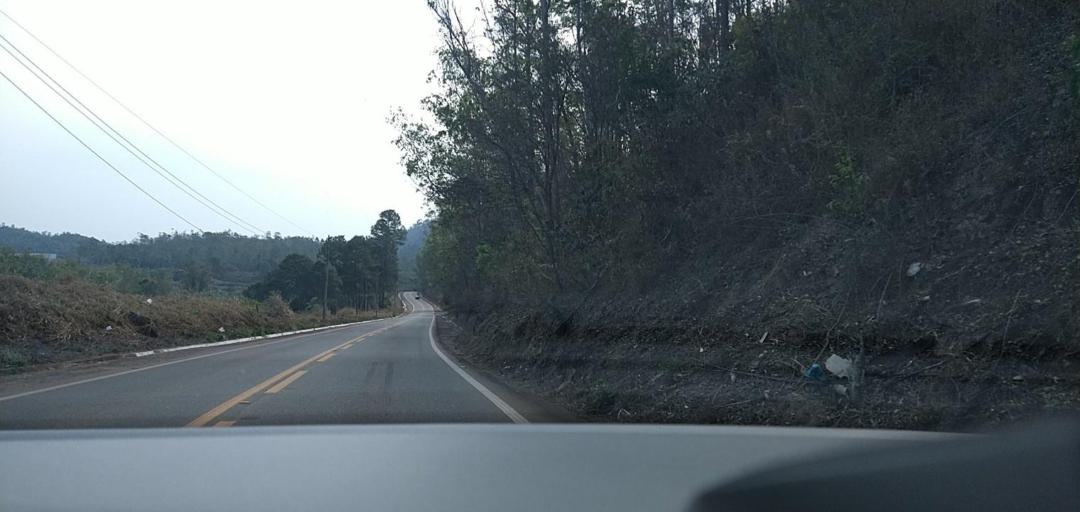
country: BR
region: Minas Gerais
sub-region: Rio Piracicaba
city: Rio Piracicaba
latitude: -19.8763
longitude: -43.1222
